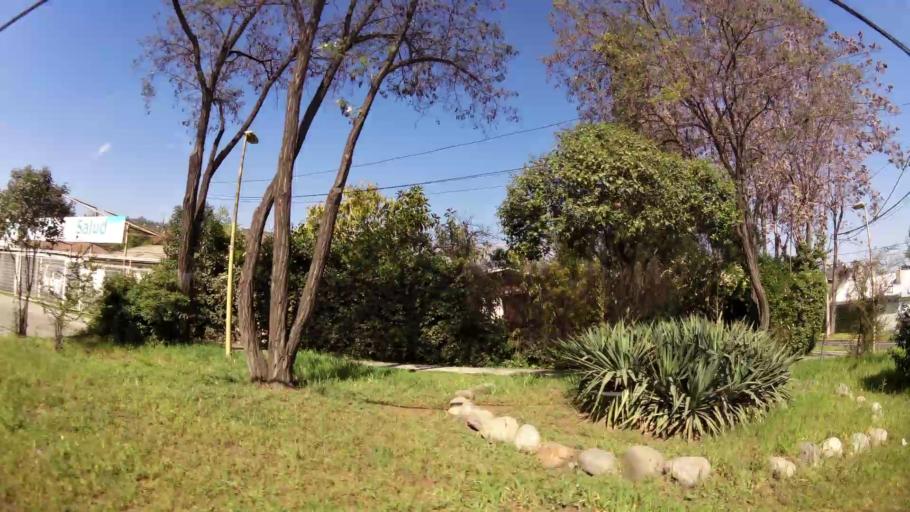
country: CL
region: Santiago Metropolitan
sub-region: Provincia de Santiago
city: Villa Presidente Frei, Nunoa, Santiago, Chile
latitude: -33.3982
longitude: -70.5460
